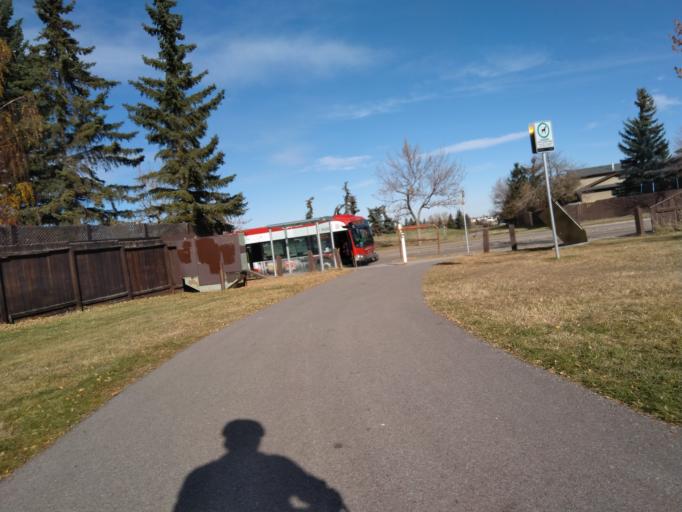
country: CA
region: Alberta
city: Calgary
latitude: 51.1296
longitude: -114.0833
